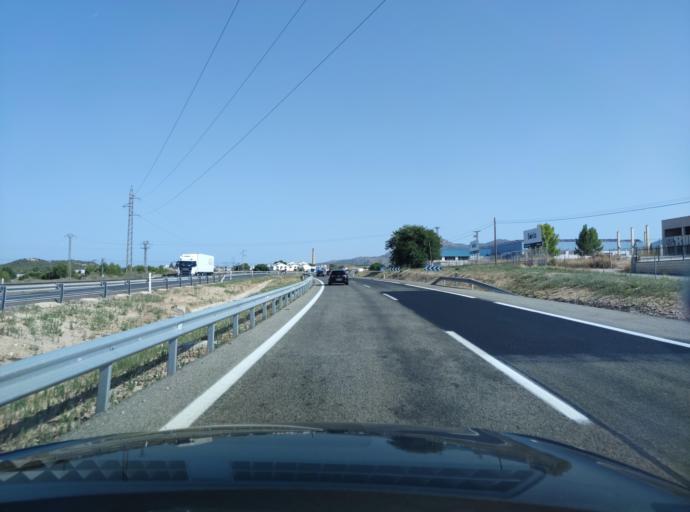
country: ES
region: Valencia
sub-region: Provincia de Alicante
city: Sax
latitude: 38.5391
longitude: -0.8104
